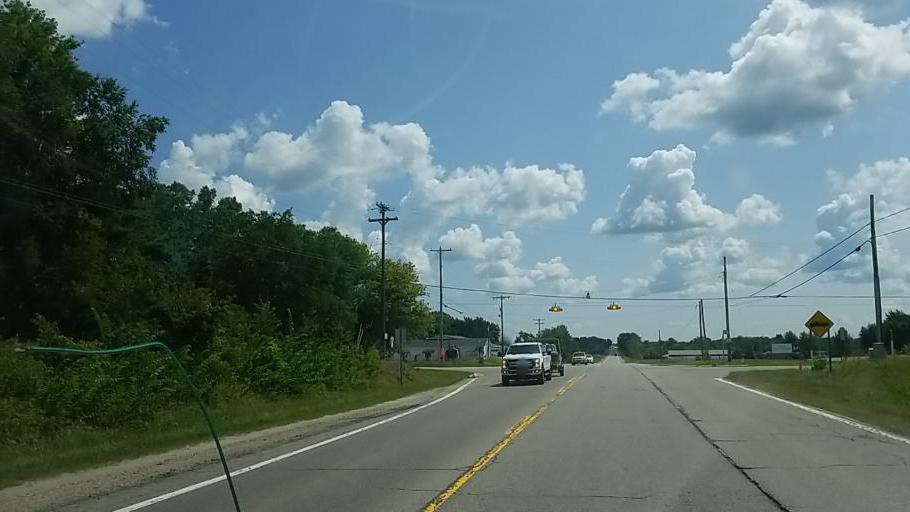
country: US
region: Michigan
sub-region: Muskegon County
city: Ravenna
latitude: 43.2352
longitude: -85.9485
